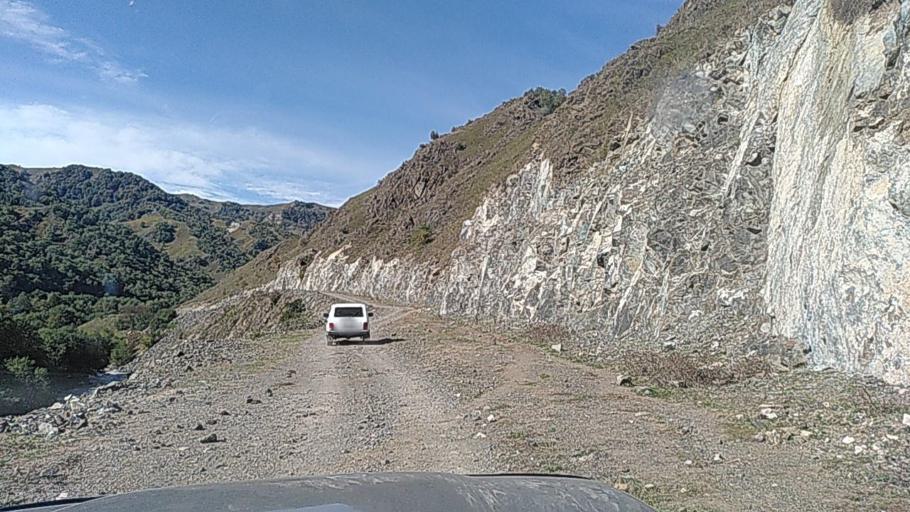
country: RU
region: Kabardino-Balkariya
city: Kamennomostskoye
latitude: 43.7209
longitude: 42.8928
